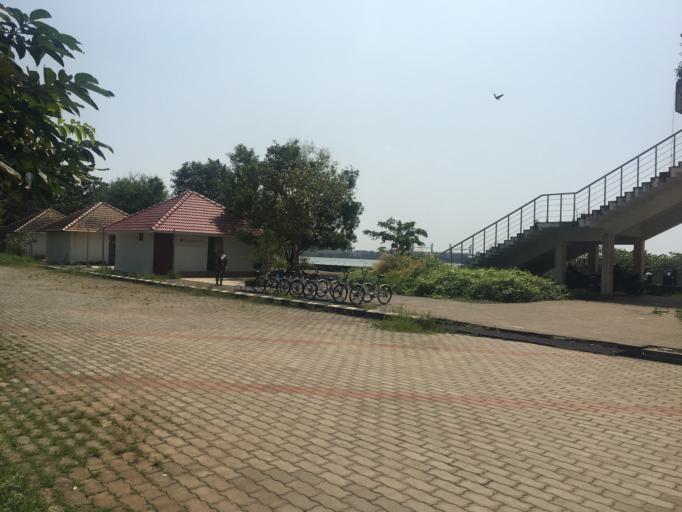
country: IN
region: Kerala
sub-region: Ernakulam
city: Cochin
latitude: 9.9725
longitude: 76.2787
